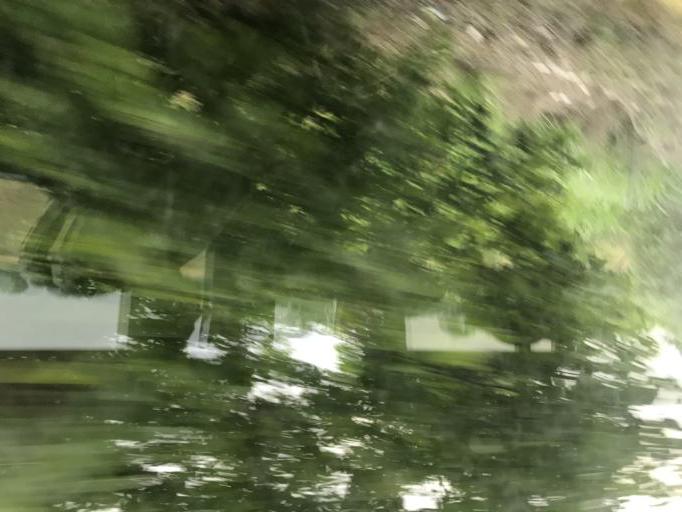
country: GR
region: East Macedonia and Thrace
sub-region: Nomos Rodopis
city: Aratos
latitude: 41.0800
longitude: 25.5599
